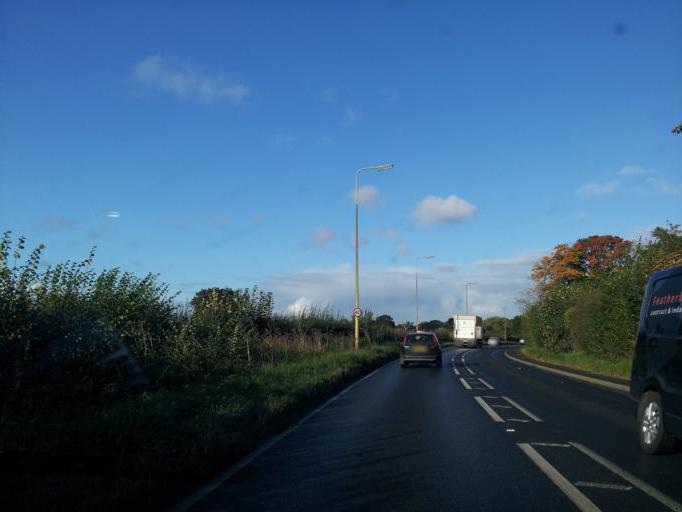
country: GB
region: England
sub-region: Norfolk
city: King's Lynn
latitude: 52.7165
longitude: 0.4540
